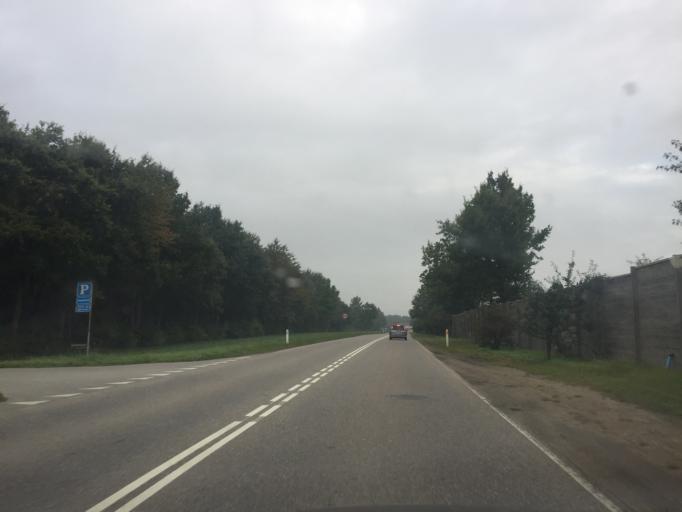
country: DK
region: Capital Region
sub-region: Hoje-Taastrup Kommune
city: Flong
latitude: 55.6437
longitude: 12.1910
